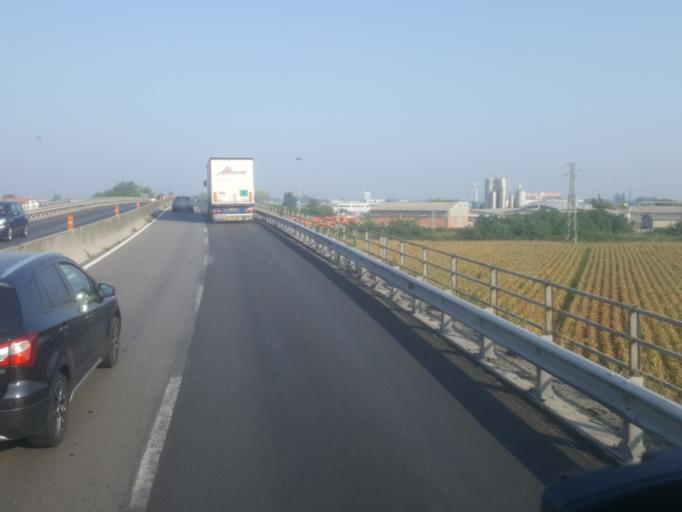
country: IT
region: Emilia-Romagna
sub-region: Provincia di Ravenna
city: Fornace Zarattini
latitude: 44.4203
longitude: 12.1651
